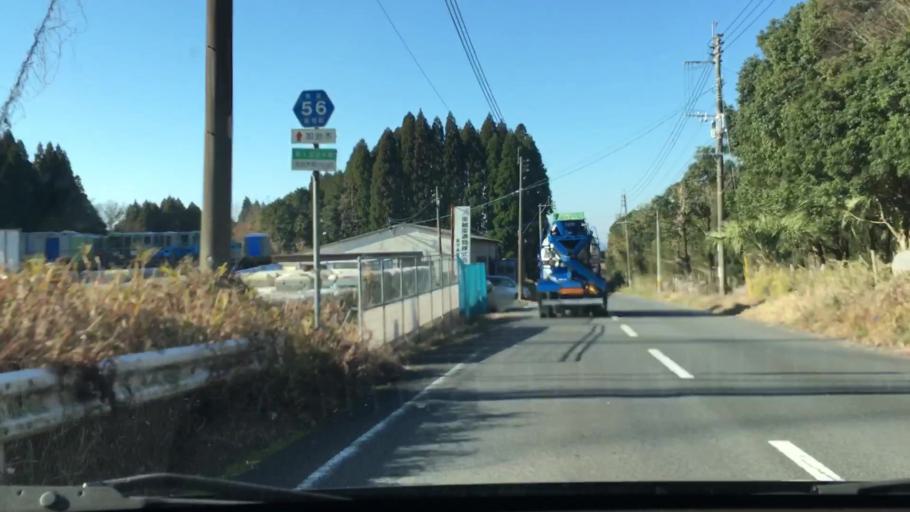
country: JP
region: Kagoshima
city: Kajiki
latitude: 31.7728
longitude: 130.6985
